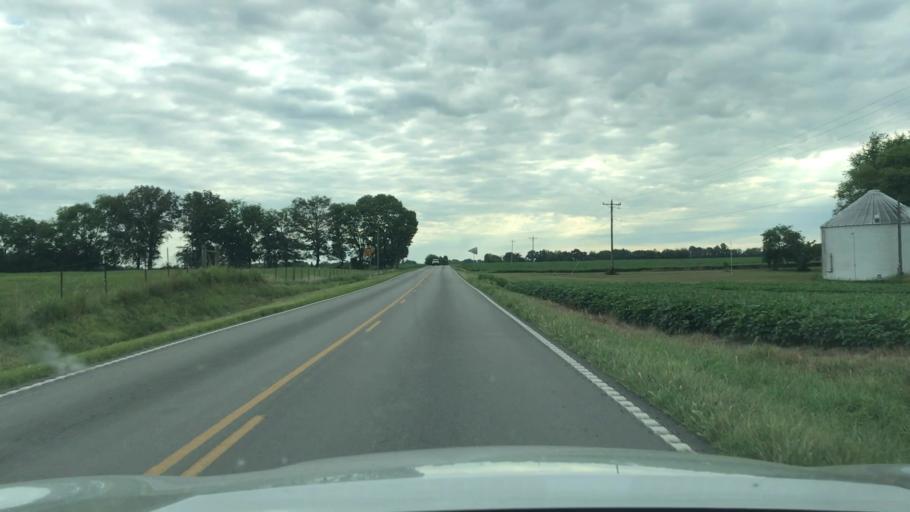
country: US
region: Kentucky
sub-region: Todd County
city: Elkton
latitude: 36.7375
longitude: -87.1853
